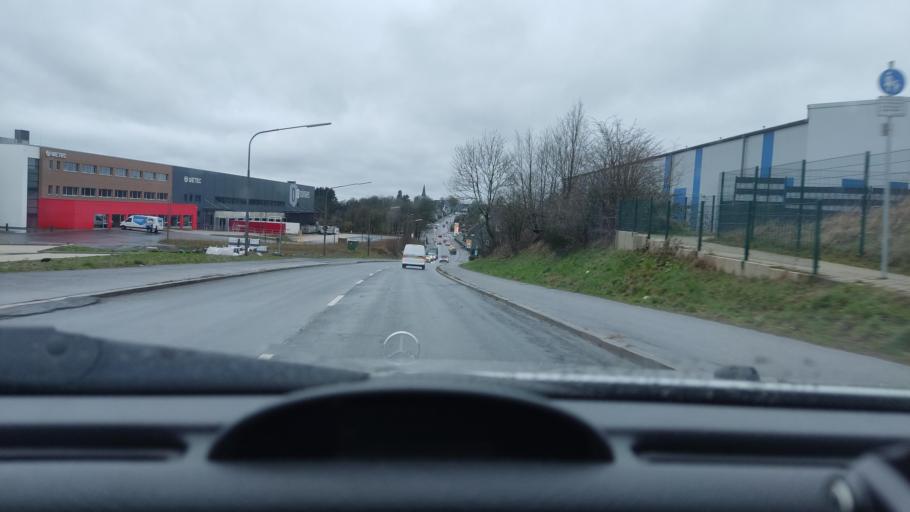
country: DE
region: North Rhine-Westphalia
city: Wermelskirchen
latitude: 51.1378
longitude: 7.1947
